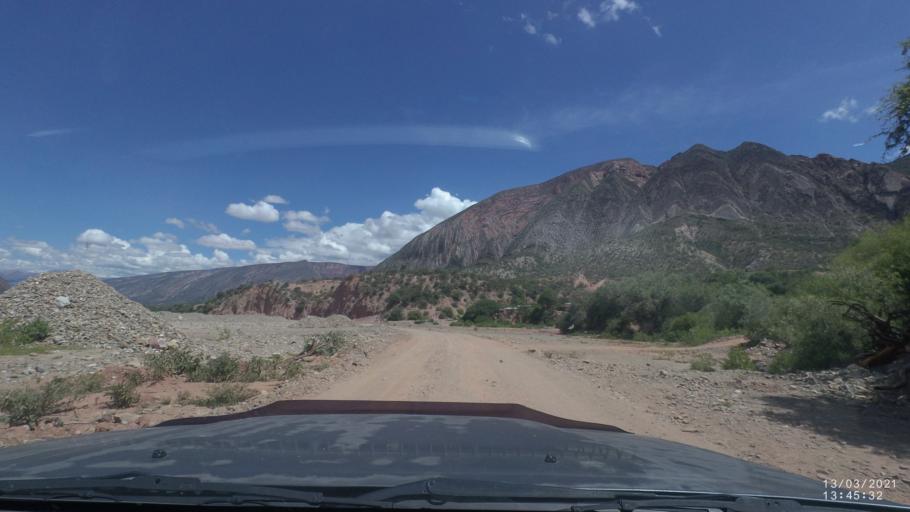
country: BO
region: Cochabamba
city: Cliza
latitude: -17.9254
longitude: -65.8722
